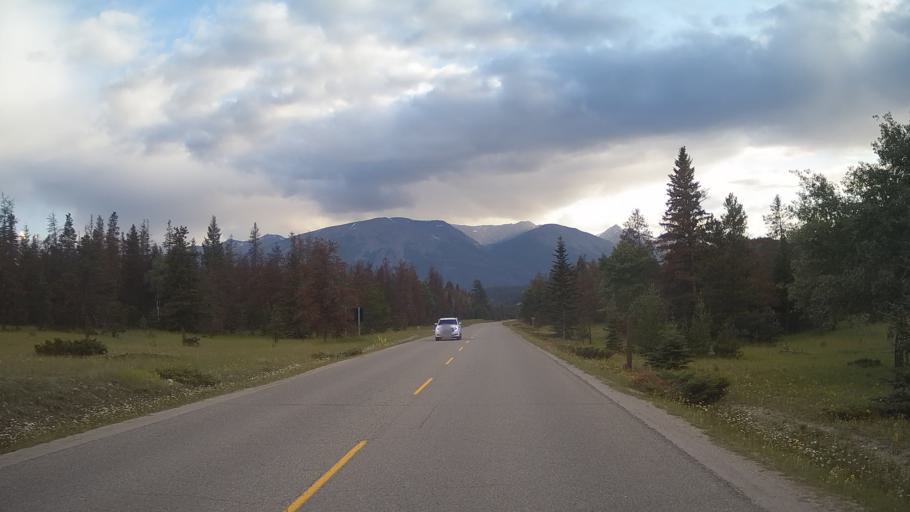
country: CA
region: Alberta
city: Jasper Park Lodge
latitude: 52.9160
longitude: -118.0467
